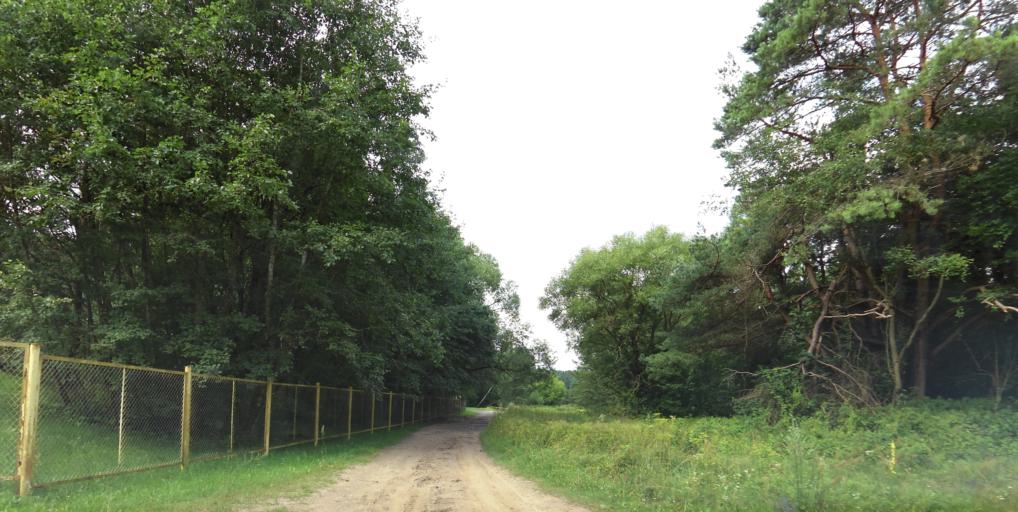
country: LT
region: Vilnius County
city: Pilaite
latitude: 54.6988
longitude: 25.1944
